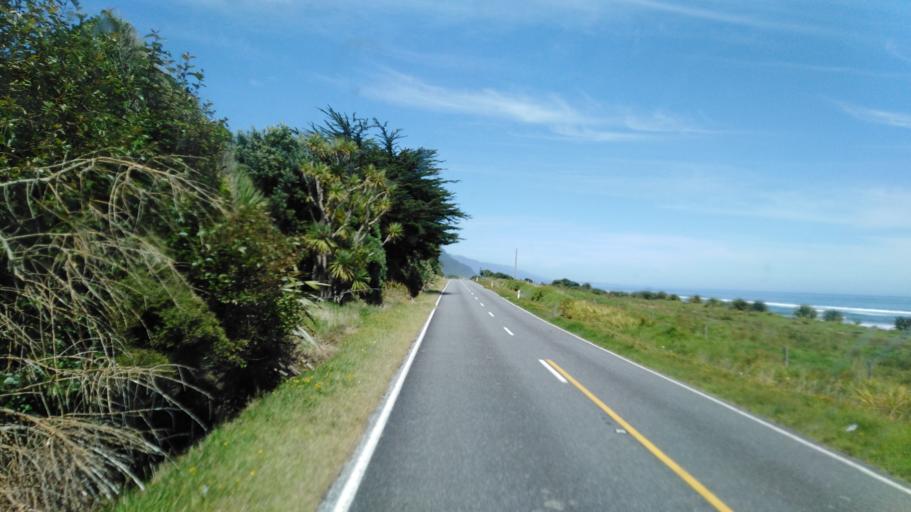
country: NZ
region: West Coast
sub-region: Buller District
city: Westport
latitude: -41.5799
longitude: 171.8989
